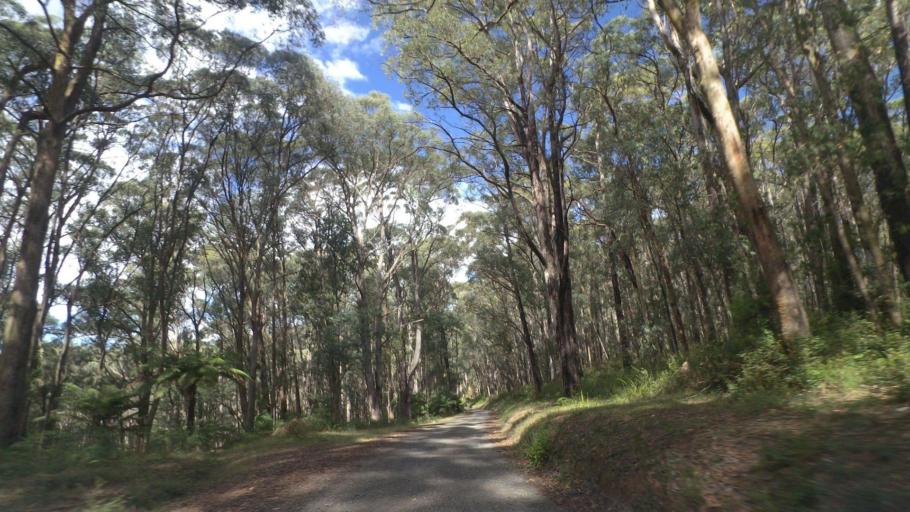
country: AU
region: Victoria
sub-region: Cardinia
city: Gembrook
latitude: -37.9086
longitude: 145.6143
